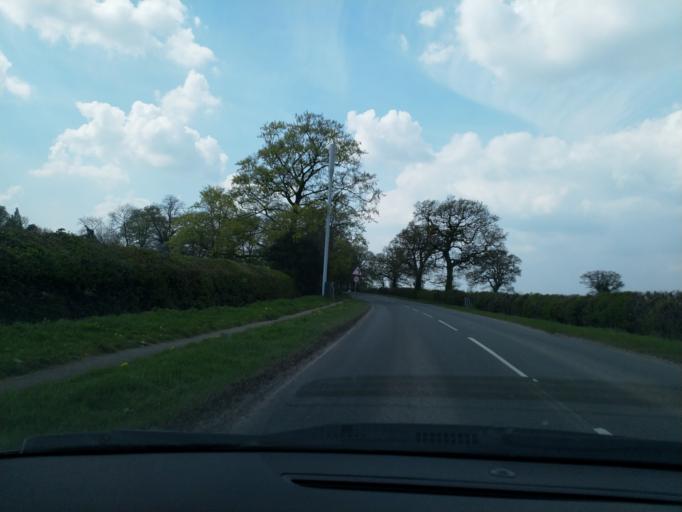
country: GB
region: England
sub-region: Warwickshire
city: Royal Leamington Spa
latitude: 52.3176
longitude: -1.5213
